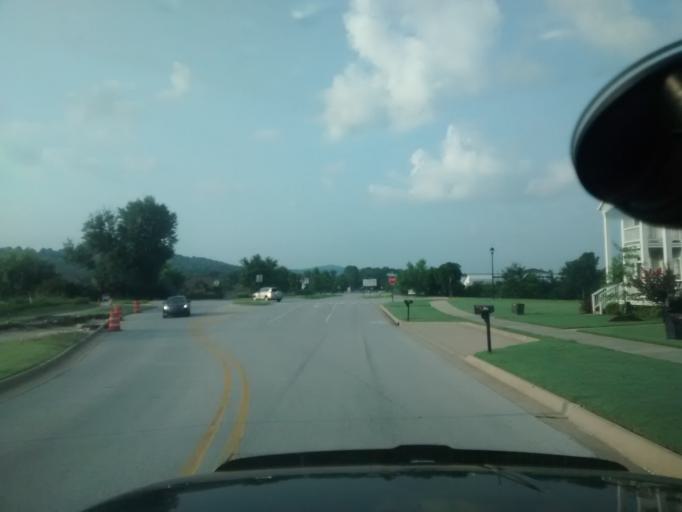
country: US
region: Arkansas
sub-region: Washington County
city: Farmington
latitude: 36.0721
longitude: -94.2177
